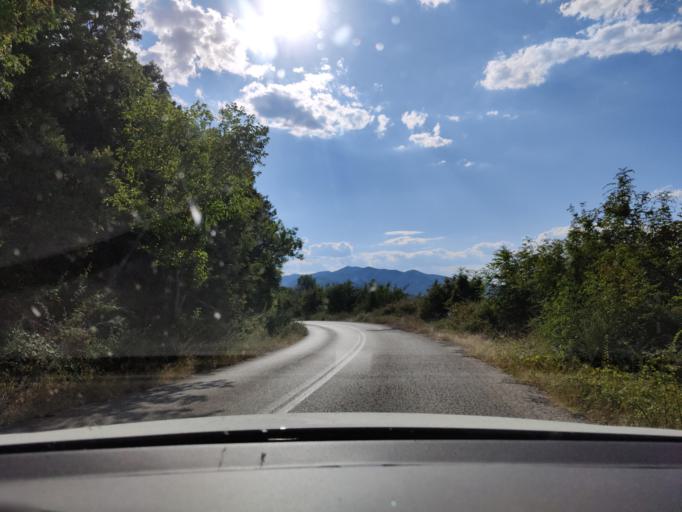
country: GR
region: Central Macedonia
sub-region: Nomos Serron
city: Chrysochorafa
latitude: 41.1806
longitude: 23.1466
